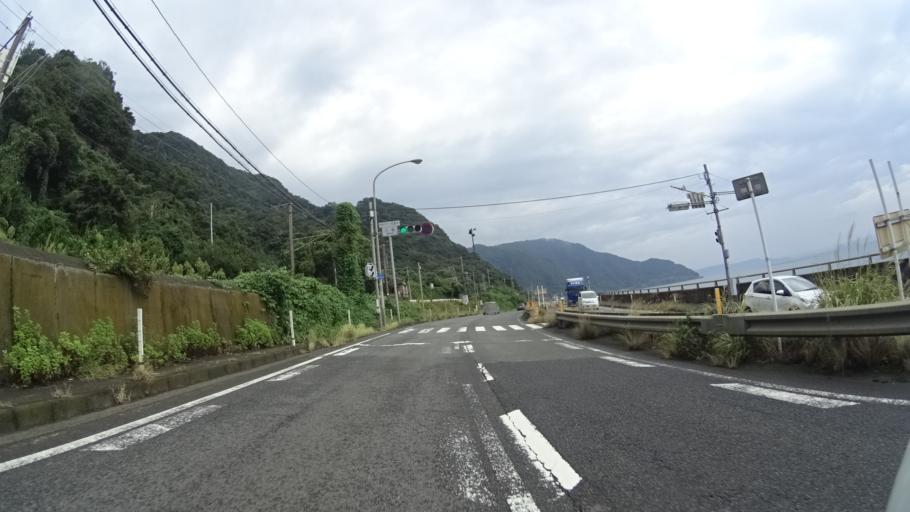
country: JP
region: Kagoshima
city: Kagoshima-shi
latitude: 31.6338
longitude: 130.6017
